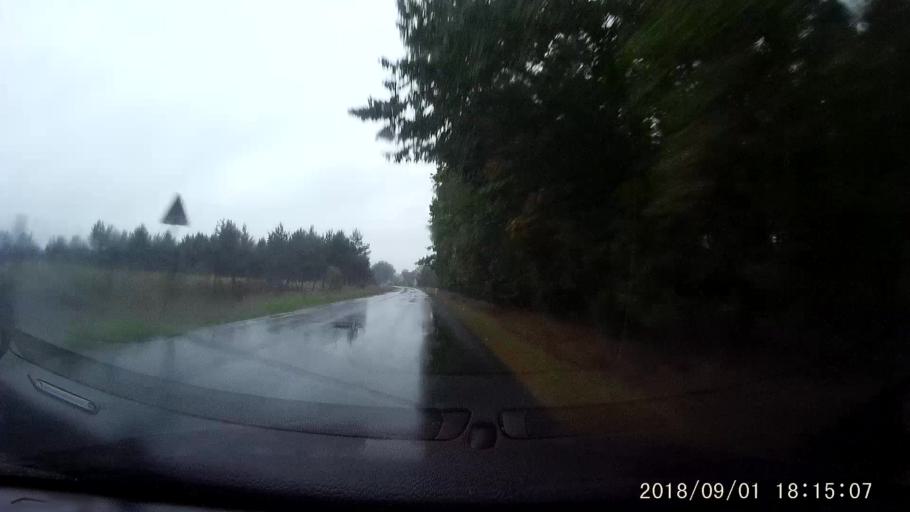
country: PL
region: Lower Silesian Voivodeship
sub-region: Powiat zgorzelecki
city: Piensk
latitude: 51.2847
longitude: 15.0575
